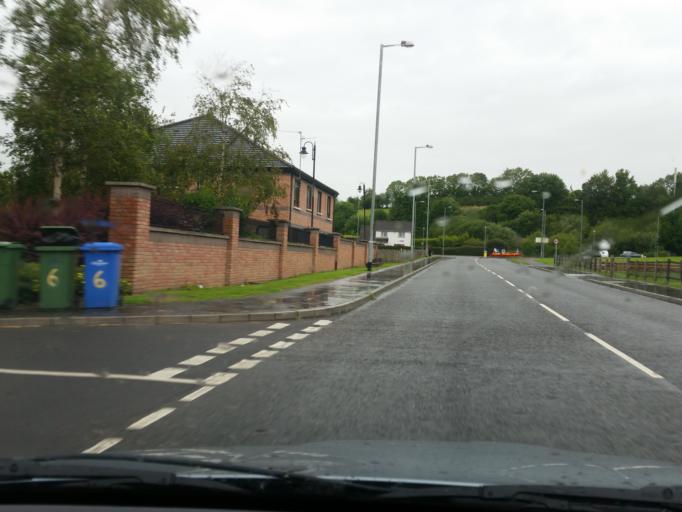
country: GB
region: Northern Ireland
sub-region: Fermanagh District
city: Enniskillen
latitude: 54.3322
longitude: -7.6621
